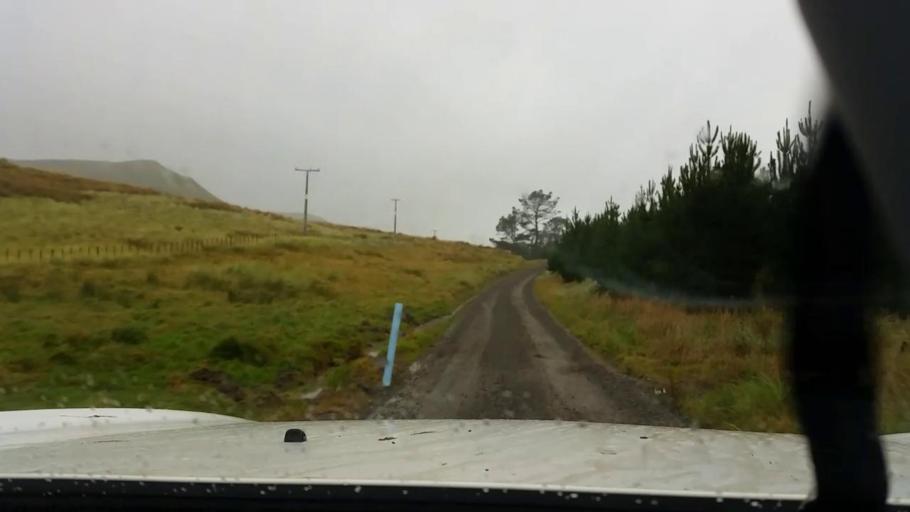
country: NZ
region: Wellington
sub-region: Masterton District
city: Masterton
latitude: -41.2529
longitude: 175.9137
